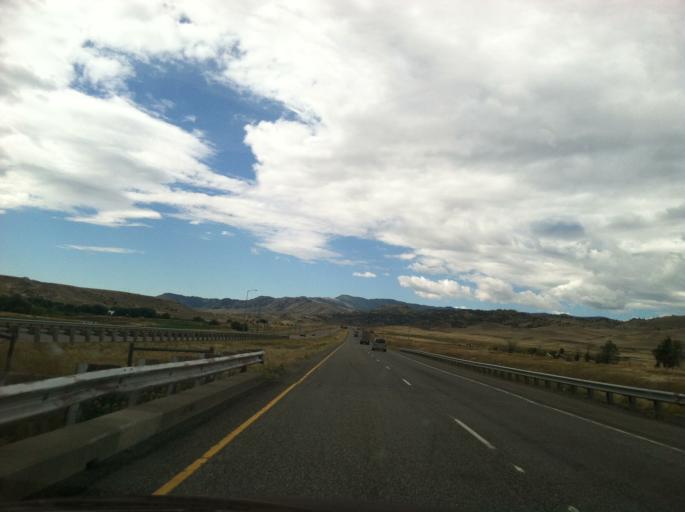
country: US
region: Montana
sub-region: Park County
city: Livingston
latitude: 45.6518
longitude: -110.6136
